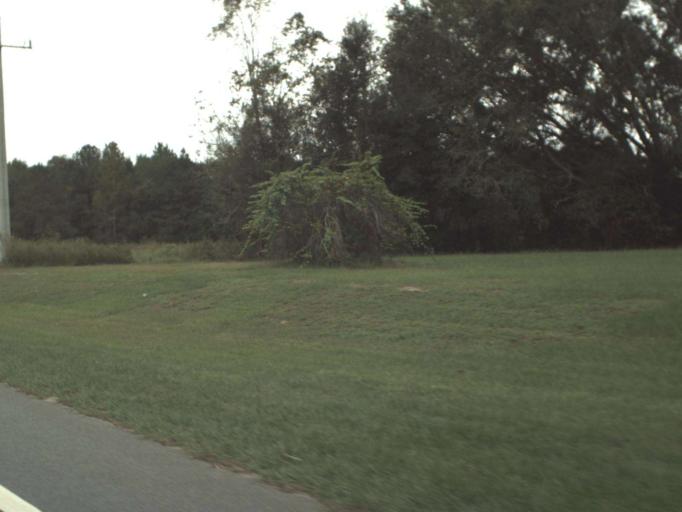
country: US
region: Florida
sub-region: Jackson County
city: Sneads
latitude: 30.7998
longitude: -85.0306
